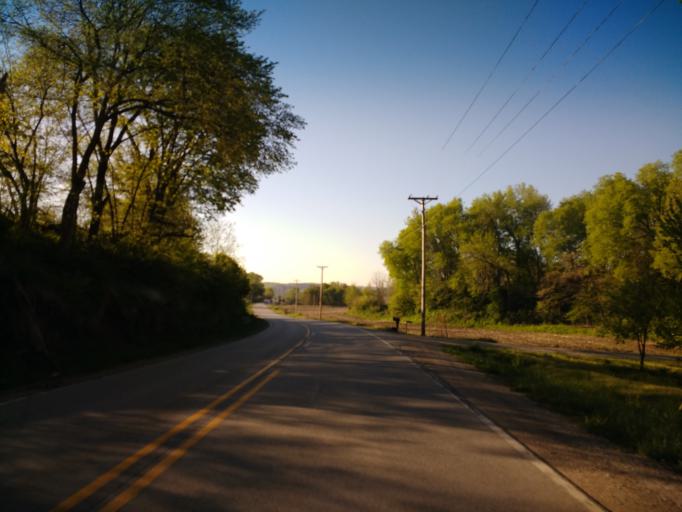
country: US
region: Iowa
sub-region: Harrison County
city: Missouri Valley
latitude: 41.4184
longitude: -95.8485
